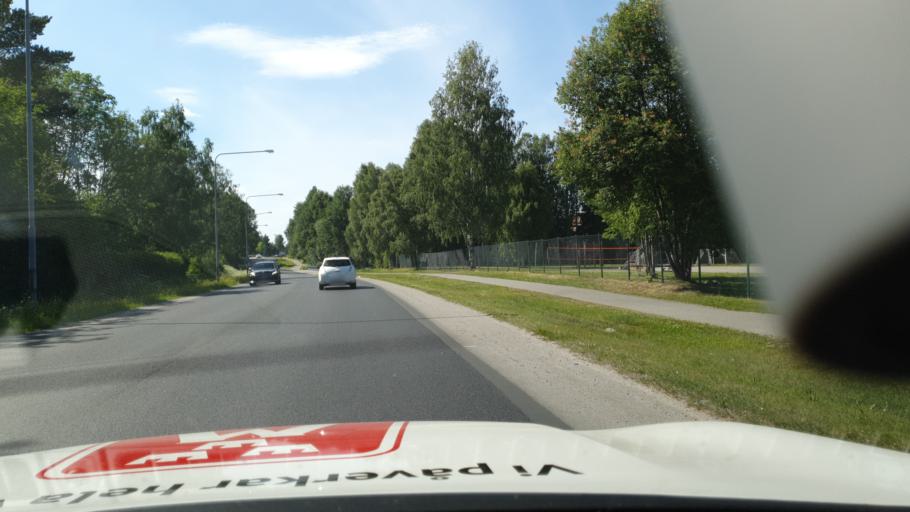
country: SE
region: Vaesterbotten
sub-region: Skelleftea Kommun
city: Viken
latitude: 64.7577
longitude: 20.9094
